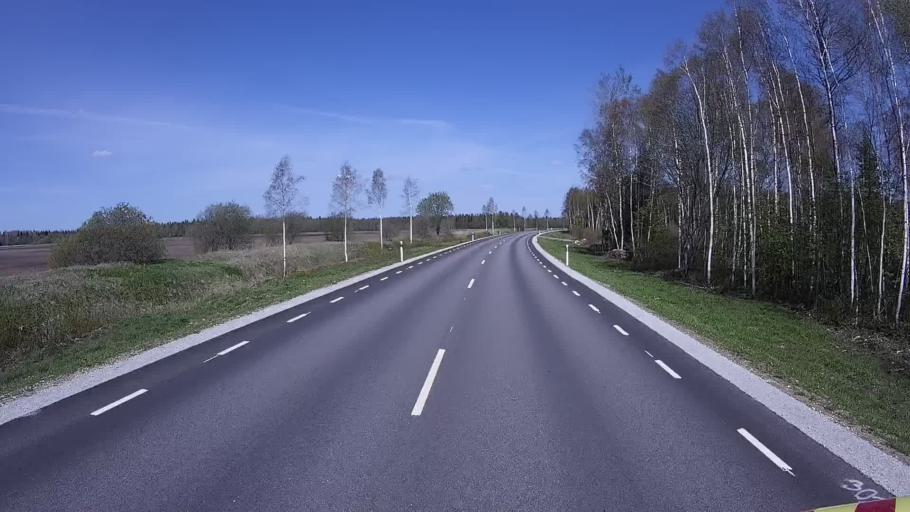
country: EE
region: Harju
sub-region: Nissi vald
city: Turba
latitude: 59.1703
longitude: 24.0745
